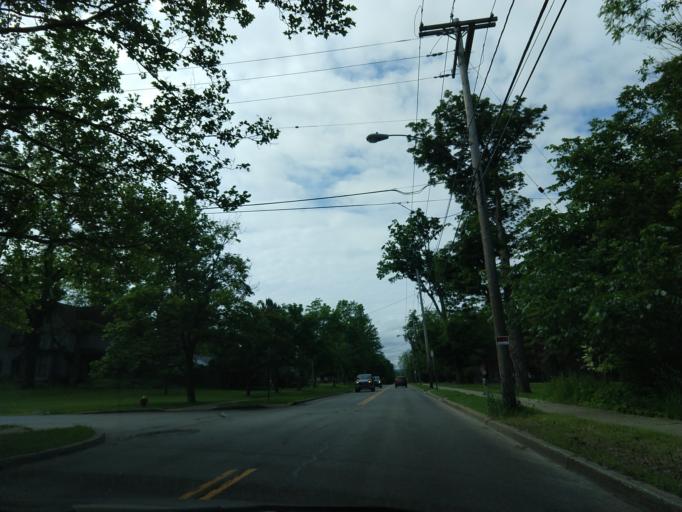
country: US
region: New York
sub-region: Erie County
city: East Aurora
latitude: 42.7619
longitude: -78.6080
